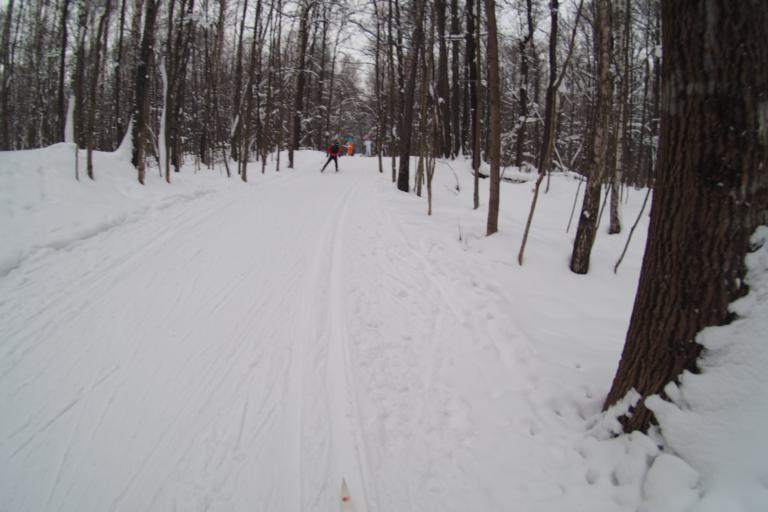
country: RU
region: Moscow
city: Ryazanskiy
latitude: 55.7684
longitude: 37.7714
